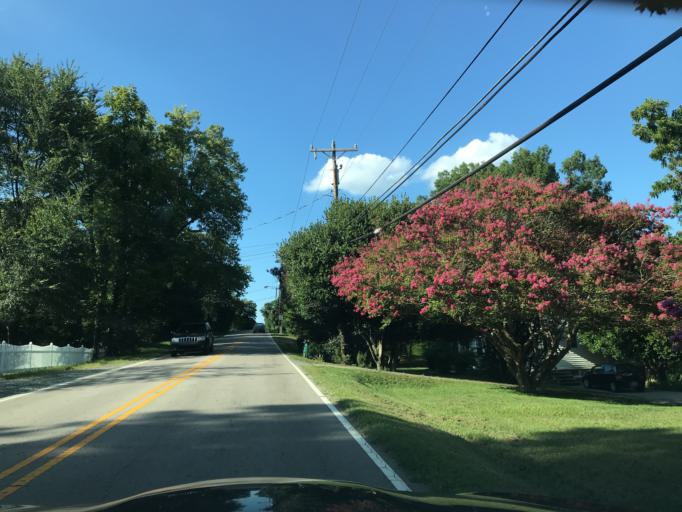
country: US
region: North Carolina
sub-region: Orange County
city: Carrboro
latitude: 35.9063
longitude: -79.0724
